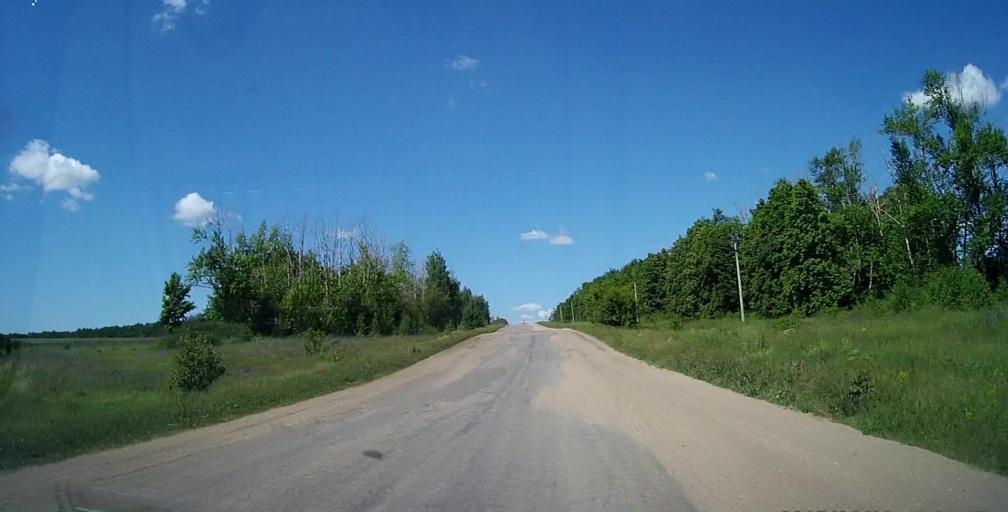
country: RU
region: Tula
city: Kurkino
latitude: 53.1843
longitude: 38.4902
